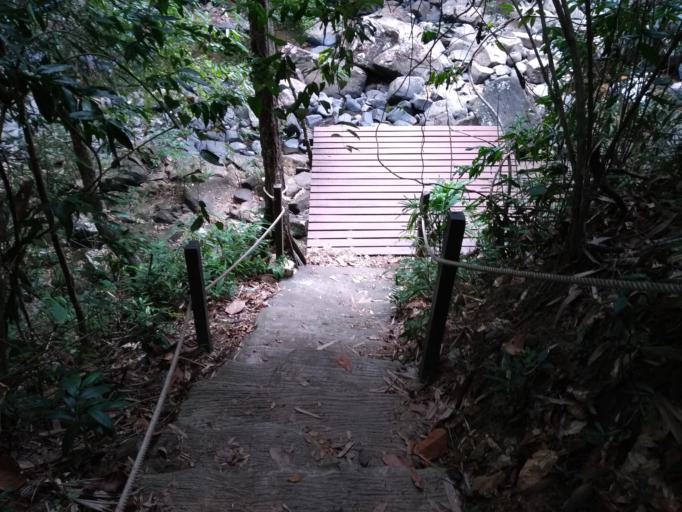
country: TH
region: Trat
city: Ko Kut
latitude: 11.6797
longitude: 102.5430
